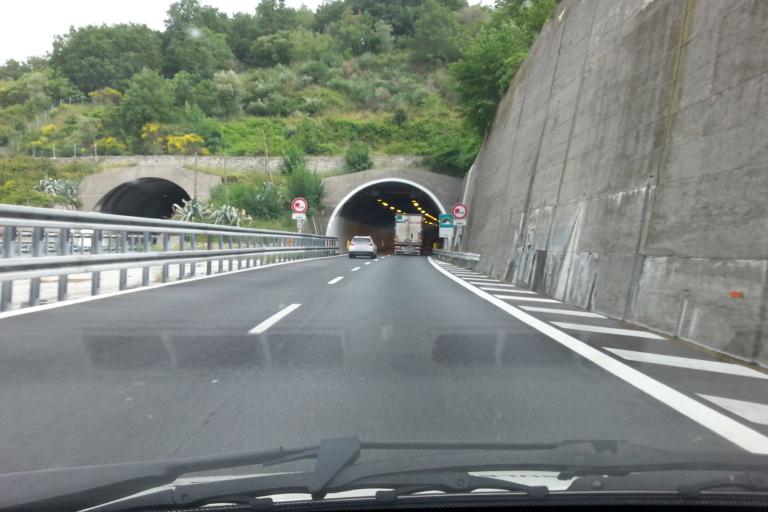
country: IT
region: Liguria
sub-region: Provincia di Savona
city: Calice Ligure
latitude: 44.1976
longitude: 8.3052
